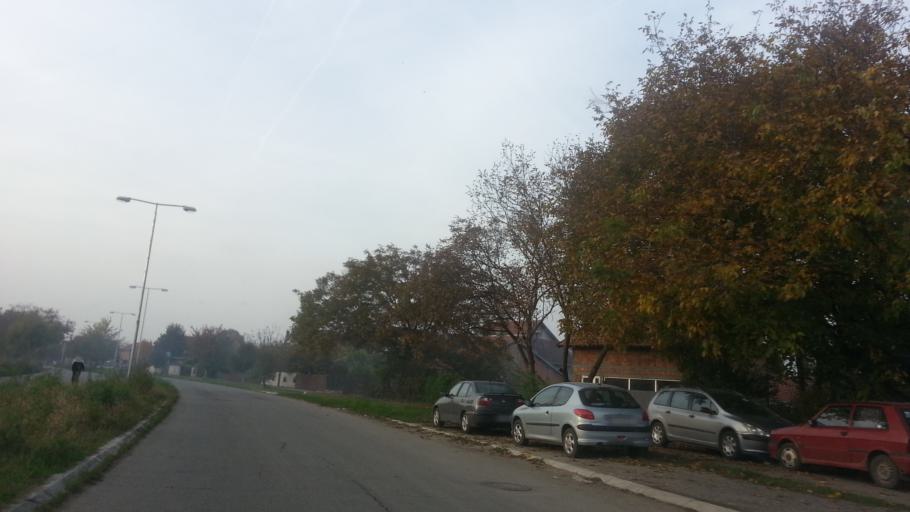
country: RS
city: Novi Banovci
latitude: 44.8977
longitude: 20.2800
